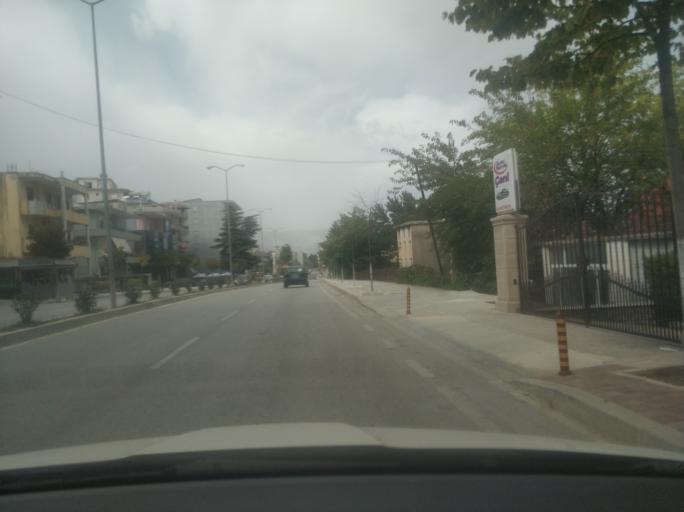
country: AL
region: Gjirokaster
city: Gjirokaster
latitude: 40.0789
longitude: 20.1497
